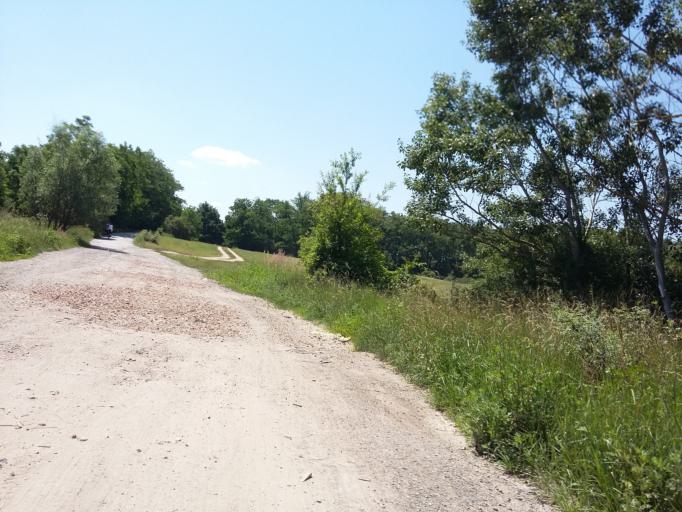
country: AT
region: Lower Austria
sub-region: Politischer Bezirk Ganserndorf
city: Marchegg
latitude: 48.2776
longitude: 16.9663
